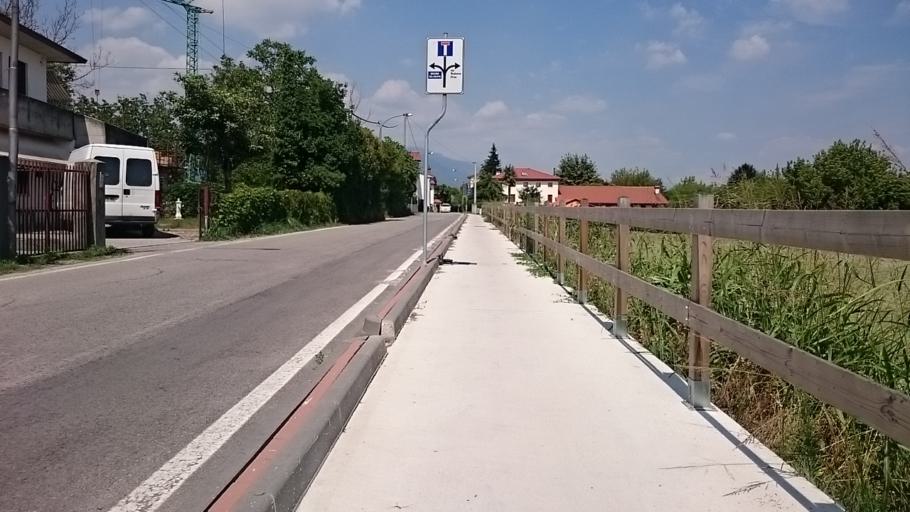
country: IT
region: Veneto
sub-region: Provincia di Vicenza
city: Bassano del Grappa
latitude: 45.7345
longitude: 11.7242
